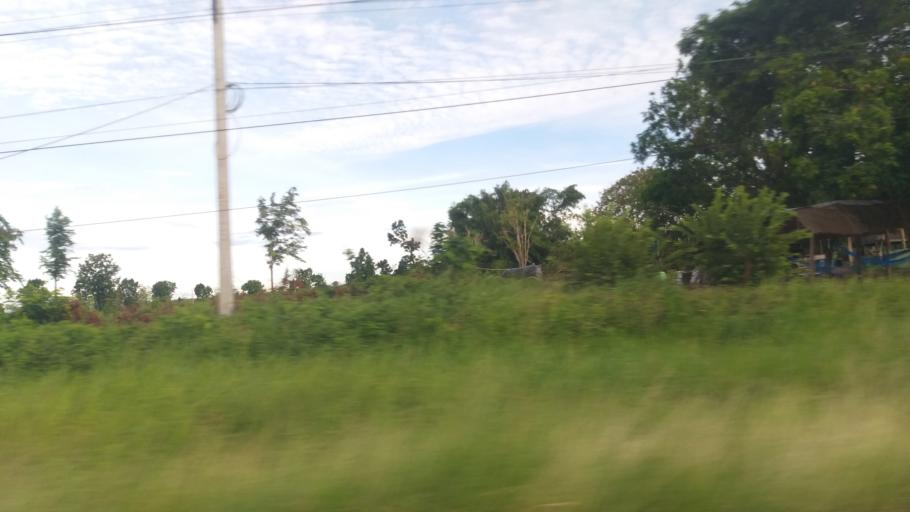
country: TH
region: Chaiyaphum
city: Phu Khiao
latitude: 16.3403
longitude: 102.2359
